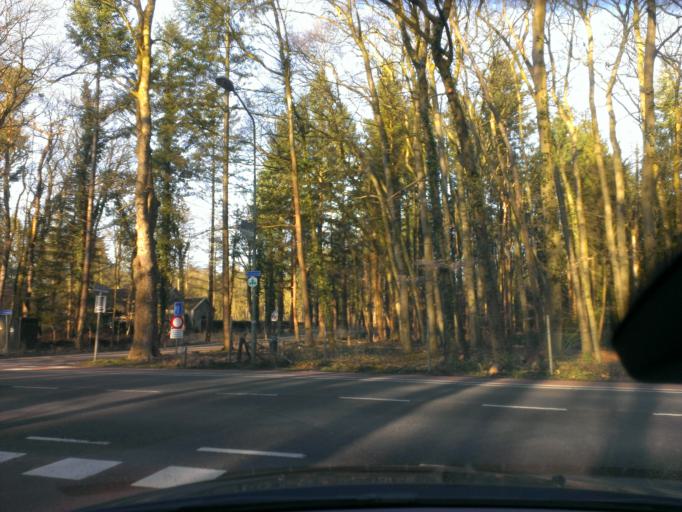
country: NL
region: Gelderland
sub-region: Gemeente Heerde
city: Heerde
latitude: 52.4244
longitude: 6.0630
